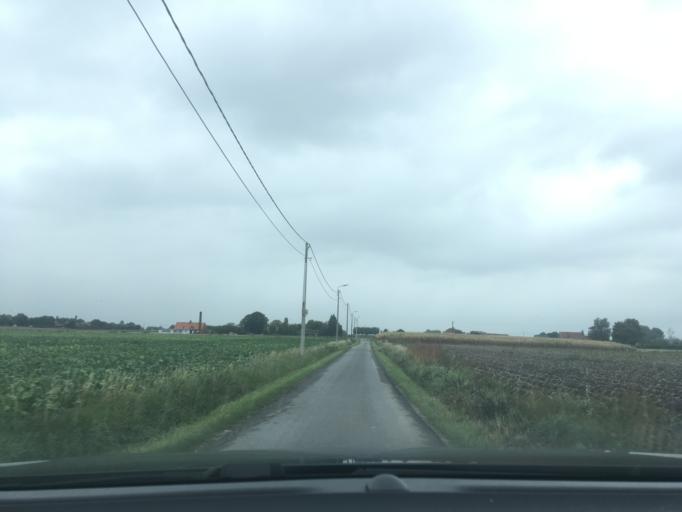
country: BE
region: Flanders
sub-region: Provincie West-Vlaanderen
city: Ledegem
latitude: 50.8834
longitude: 3.1327
